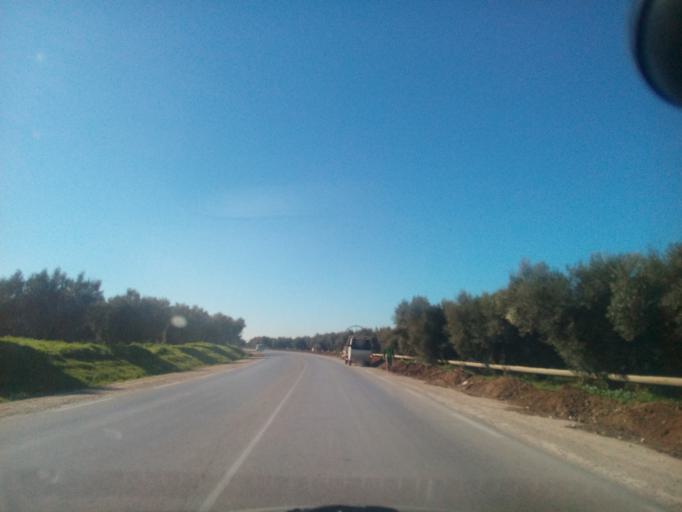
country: DZ
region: Relizane
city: Djidiouia
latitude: 35.9289
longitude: 0.8138
